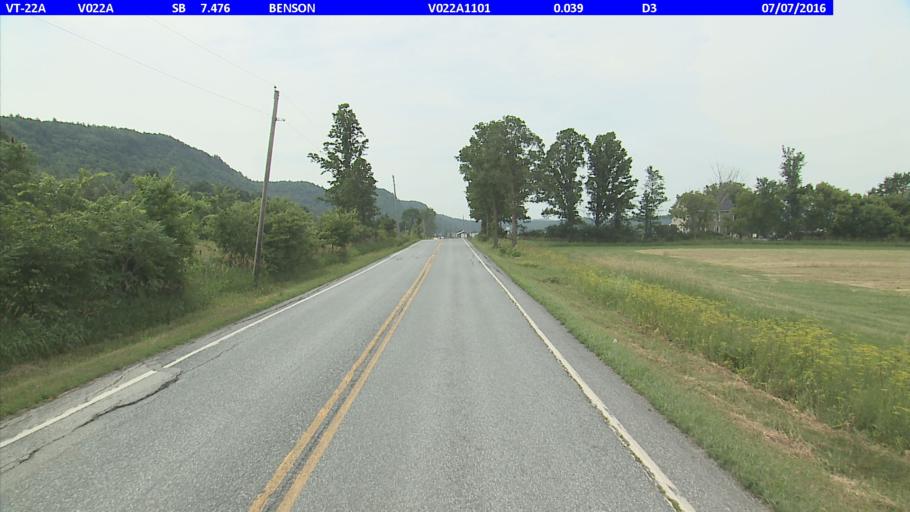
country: US
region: Vermont
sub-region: Rutland County
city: Fair Haven
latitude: 43.6699
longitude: -73.2897
